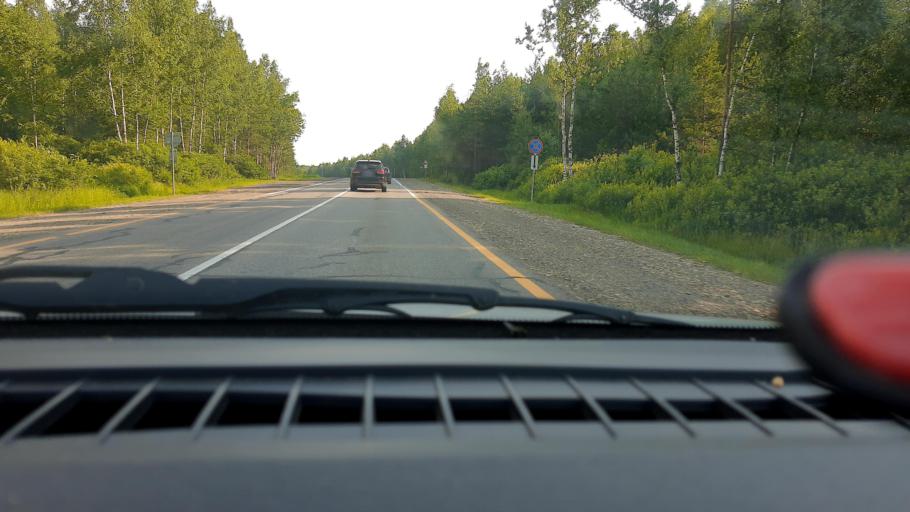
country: RU
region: Nizjnij Novgorod
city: Surovatikha
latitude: 55.7450
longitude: 43.9889
